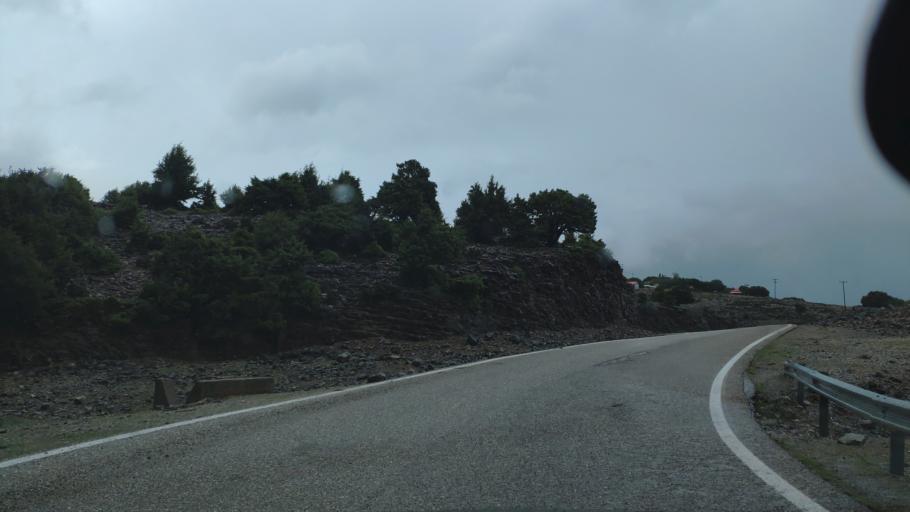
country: GR
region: West Greece
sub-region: Nomos Aitolias kai Akarnanias
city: Krikellos
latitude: 39.0752
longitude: 21.3896
